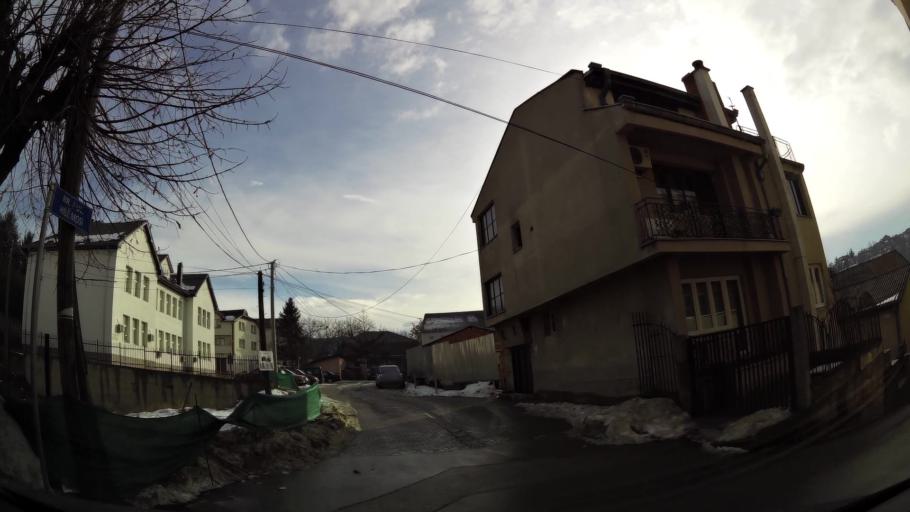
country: XK
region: Pristina
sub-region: Komuna e Prishtines
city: Pristina
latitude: 42.6674
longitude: 21.1744
